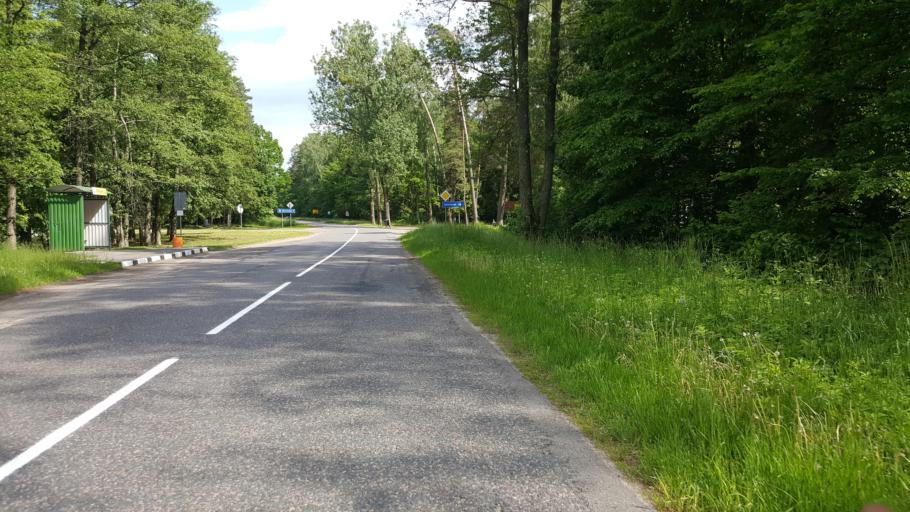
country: PL
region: Podlasie
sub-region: Powiat hajnowski
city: Bialowieza
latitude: 52.6051
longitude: 24.1078
